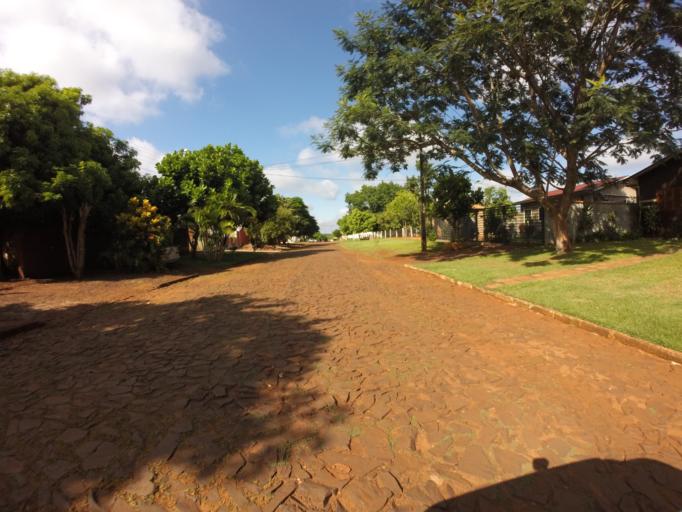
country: PY
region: Alto Parana
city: Ciudad del Este
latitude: -25.3913
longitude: -54.6409
